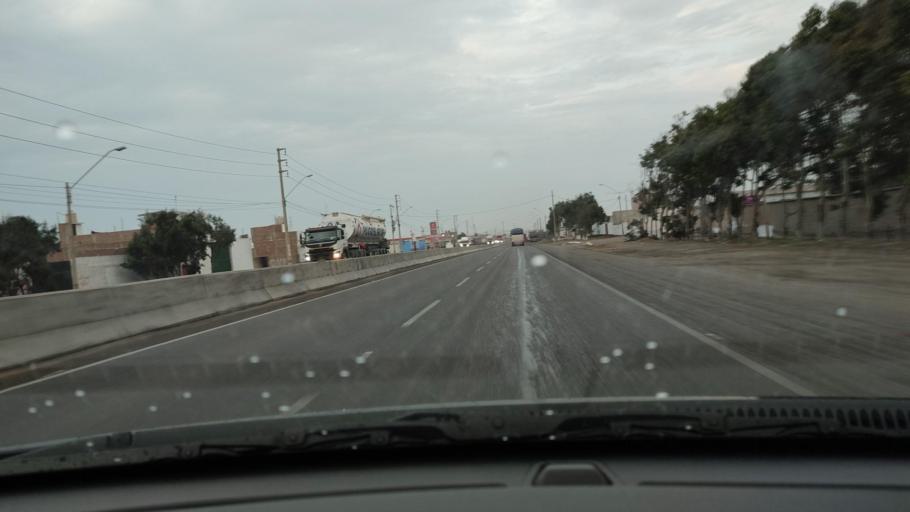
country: PE
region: La Libertad
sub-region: Provincia de Trujillo
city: Huanchaco
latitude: -8.0827
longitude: -79.0953
